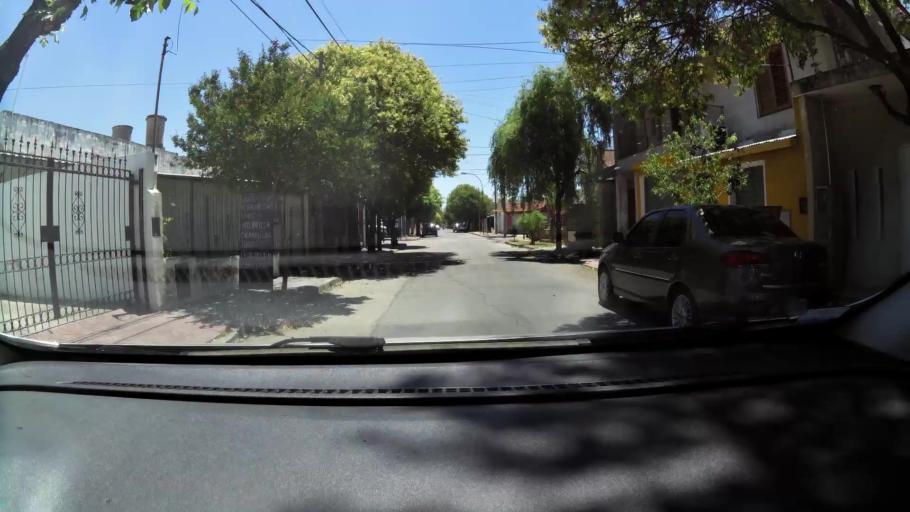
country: AR
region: Cordoba
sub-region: Departamento de Capital
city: Cordoba
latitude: -31.3867
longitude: -64.1364
